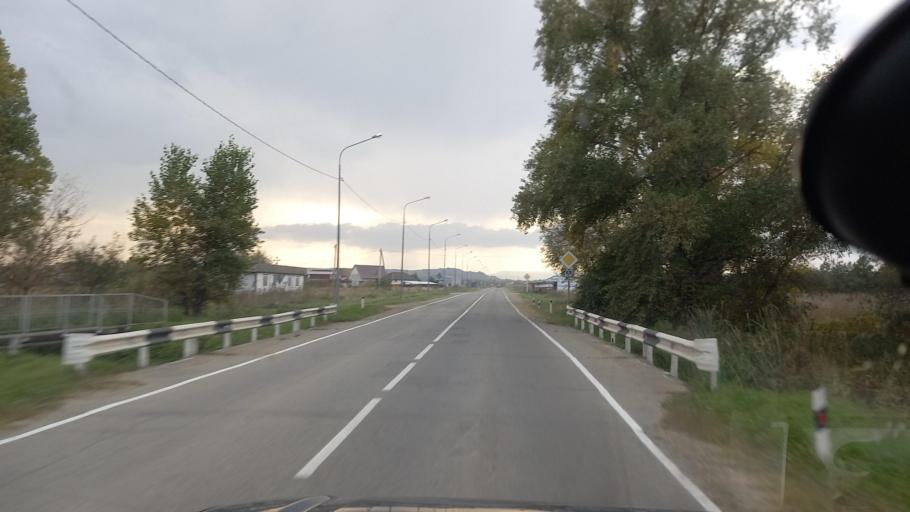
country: RU
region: Krasnodarskiy
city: Mostovskoy
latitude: 44.3961
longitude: 40.7714
